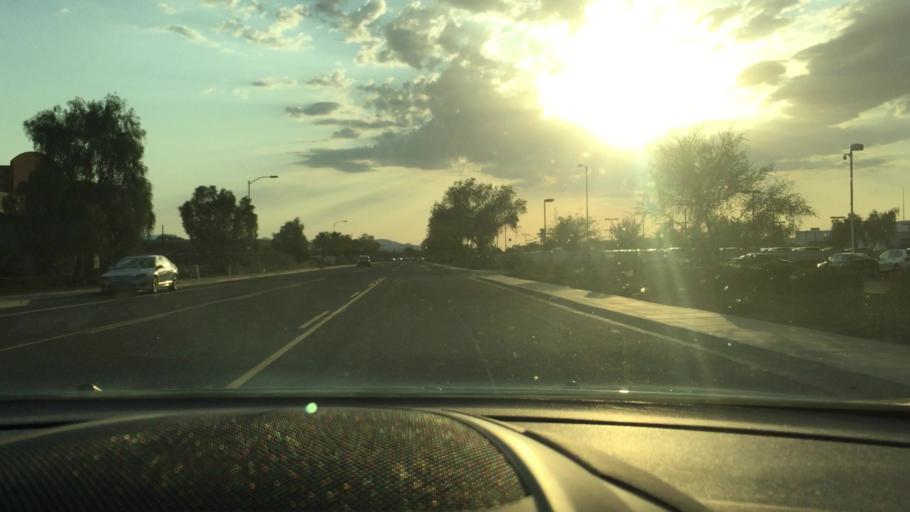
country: US
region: Arizona
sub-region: Maricopa County
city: Sun City
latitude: 33.6354
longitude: -112.2489
